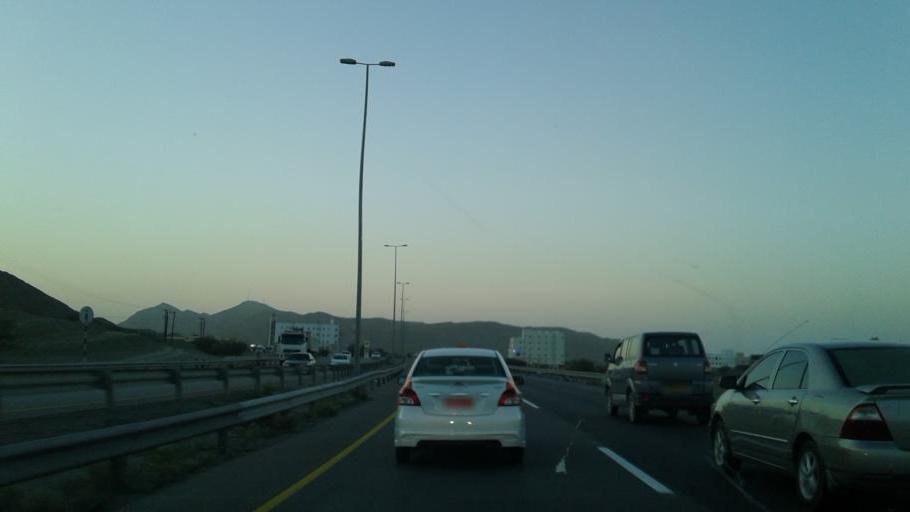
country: OM
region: Muhafazat ad Dakhiliyah
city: Bidbid
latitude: 23.5200
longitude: 58.1922
